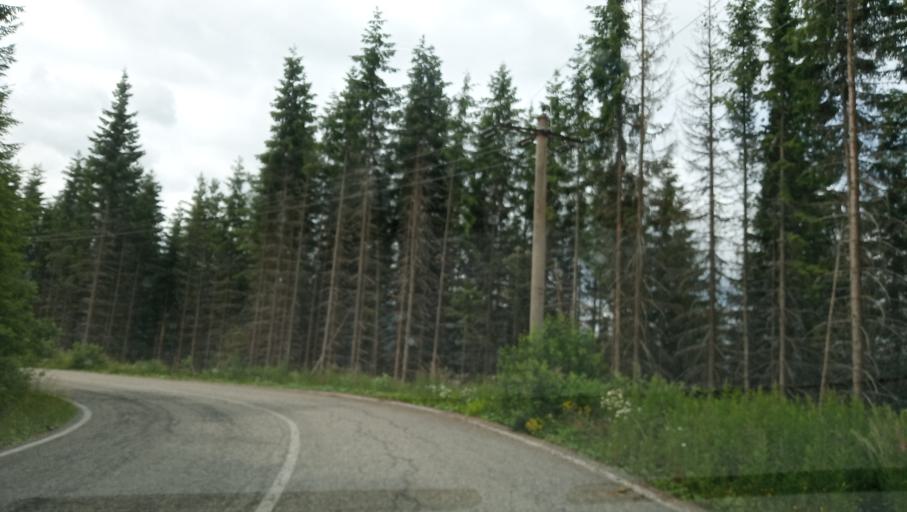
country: RO
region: Valcea
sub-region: Comuna Voineasa
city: Voineasa
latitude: 45.4280
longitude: 23.7393
